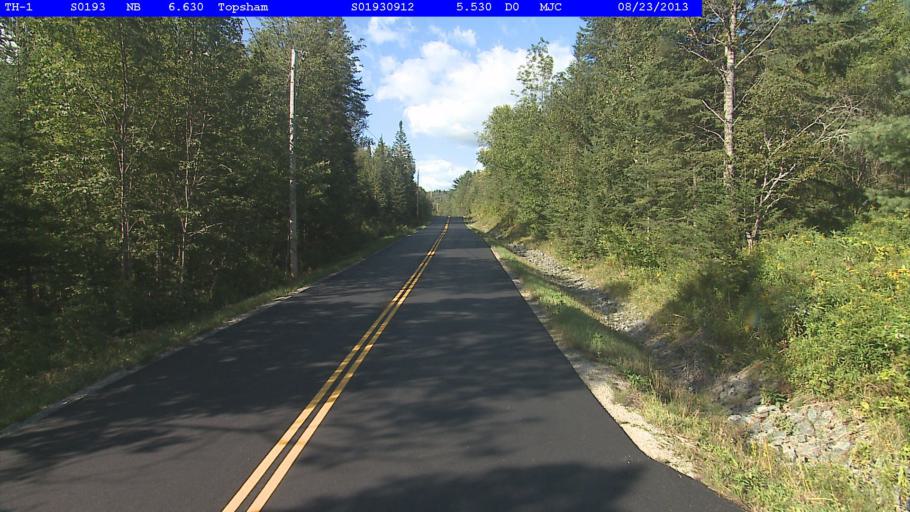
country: US
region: New Hampshire
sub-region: Grafton County
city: Woodsville
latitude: 44.1423
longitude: -72.2377
